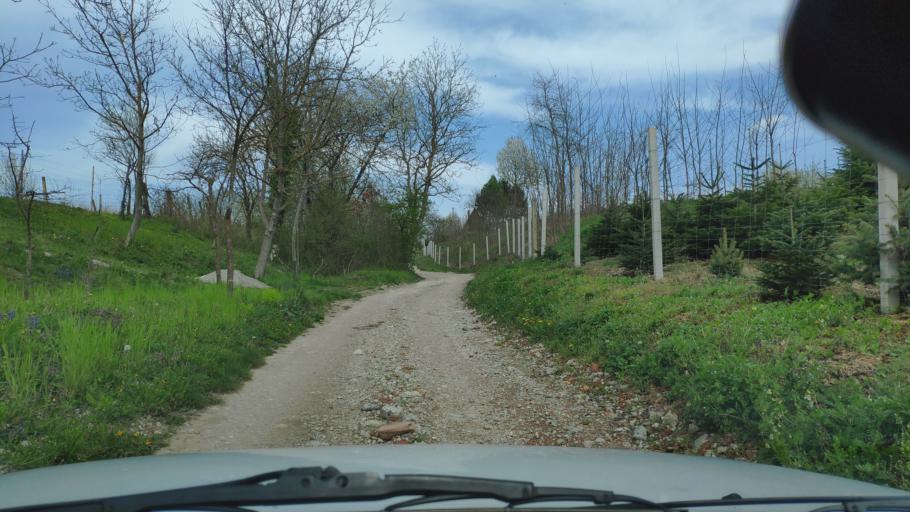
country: HU
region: Zala
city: Nagykanizsa
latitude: 46.4247
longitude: 17.0155
